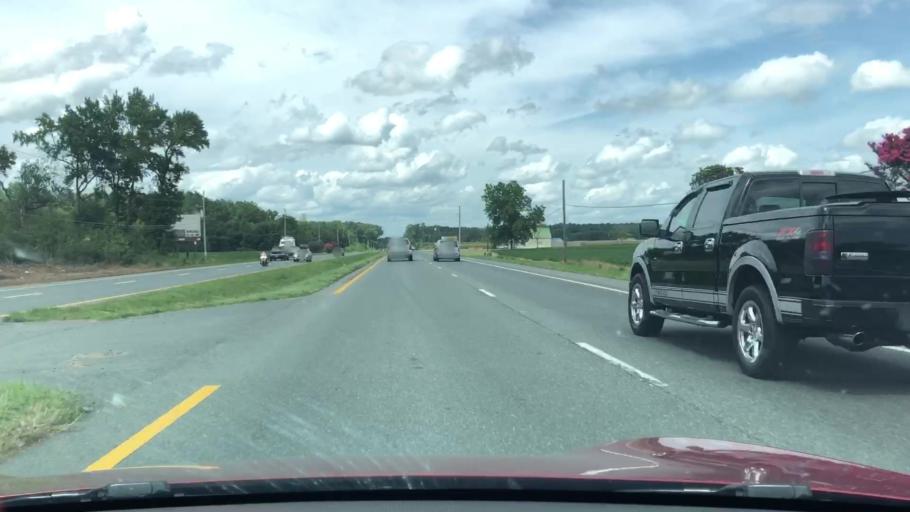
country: US
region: Virginia
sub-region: Accomack County
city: Wattsville
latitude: 37.9100
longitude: -75.5490
